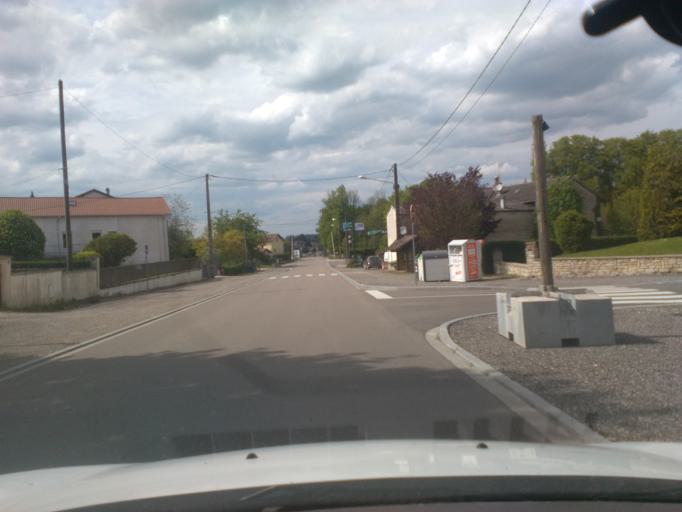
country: FR
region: Lorraine
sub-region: Departement des Vosges
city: Mirecourt
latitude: 48.2695
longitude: 6.1398
